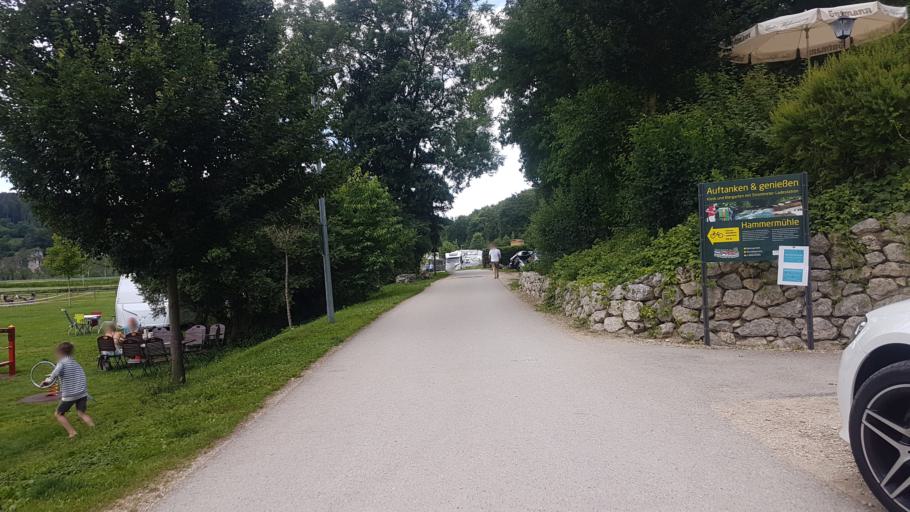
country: DE
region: Bavaria
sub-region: Regierungsbezirk Mittelfranken
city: Solnhofen
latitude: 48.8737
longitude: 11.0318
